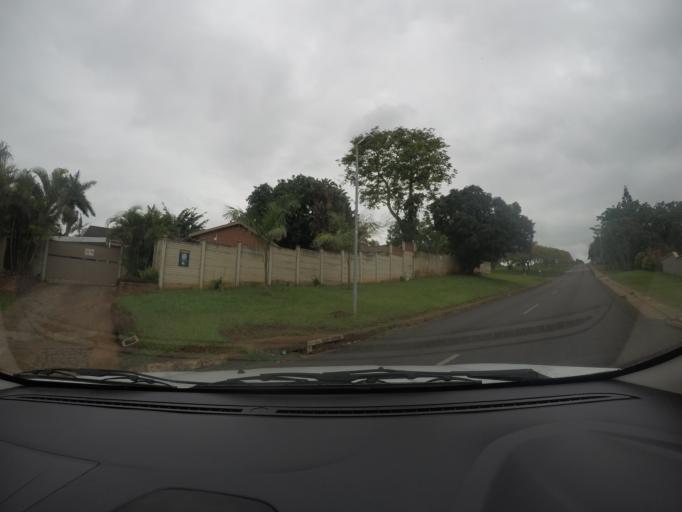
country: ZA
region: KwaZulu-Natal
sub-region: uThungulu District Municipality
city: Empangeni
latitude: -28.7608
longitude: 31.8920
